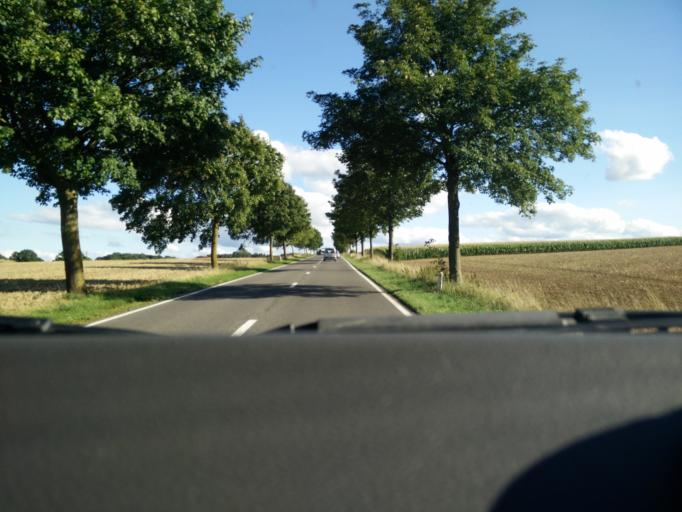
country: BE
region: Wallonia
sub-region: Province du Hainaut
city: Beaumont
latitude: 50.2549
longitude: 4.2244
